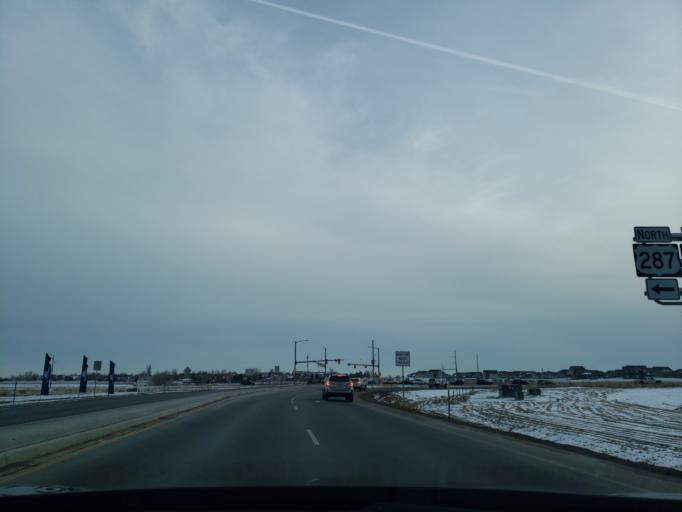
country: US
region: Colorado
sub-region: Larimer County
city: Campion
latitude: 40.3373
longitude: -105.0935
